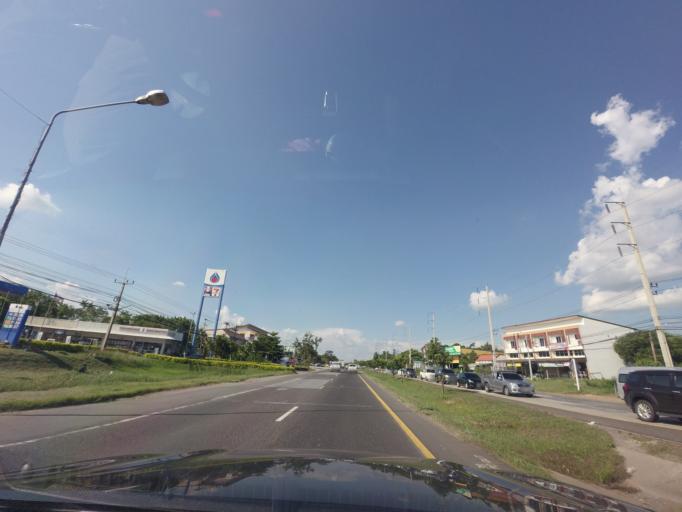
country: TH
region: Nakhon Ratchasima
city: Sida
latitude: 15.5499
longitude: 102.5484
